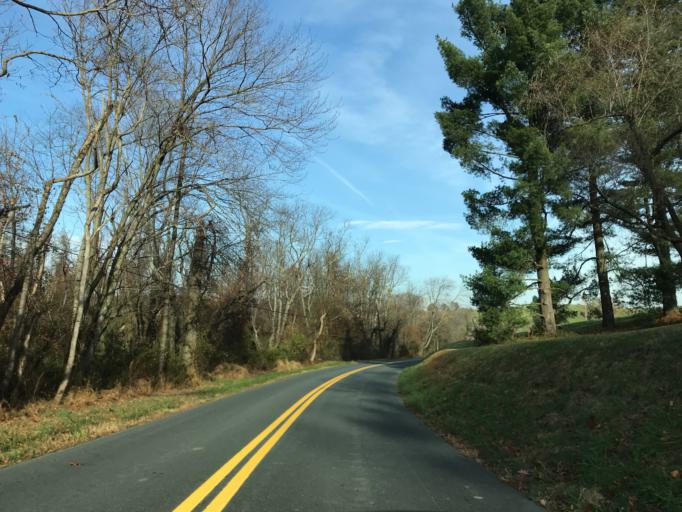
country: US
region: Maryland
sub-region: Carroll County
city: Hampstead
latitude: 39.5559
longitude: -76.7989
